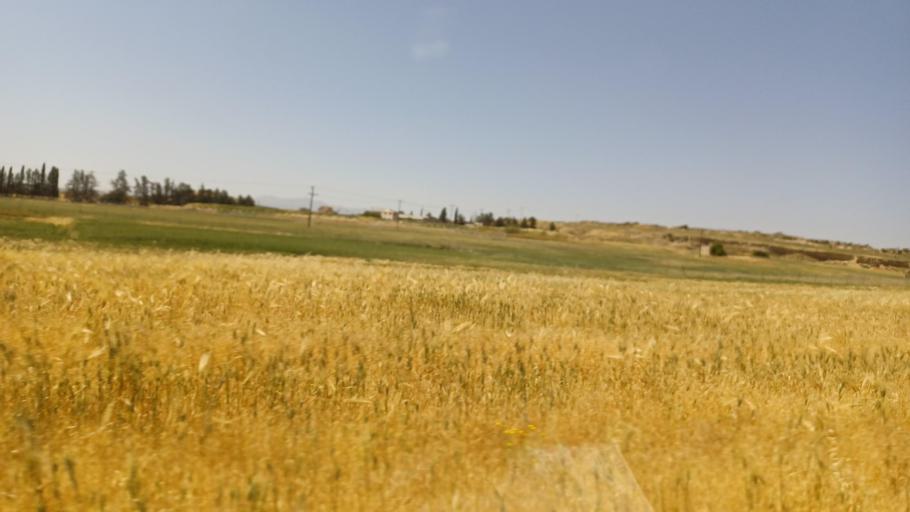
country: CY
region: Lefkosia
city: Kokkinotrimithia
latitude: 35.1554
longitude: 33.2426
